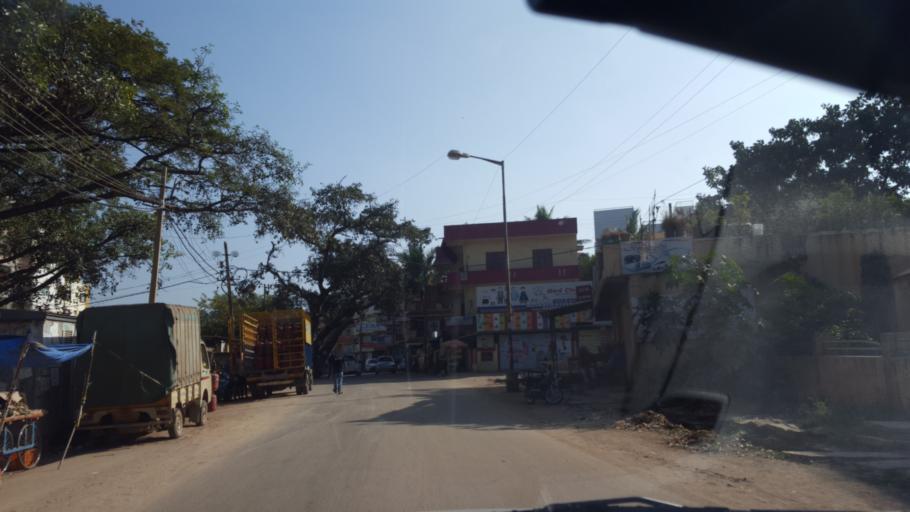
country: IN
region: Karnataka
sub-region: Bangalore Urban
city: Bangalore
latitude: 12.9514
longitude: 77.7066
